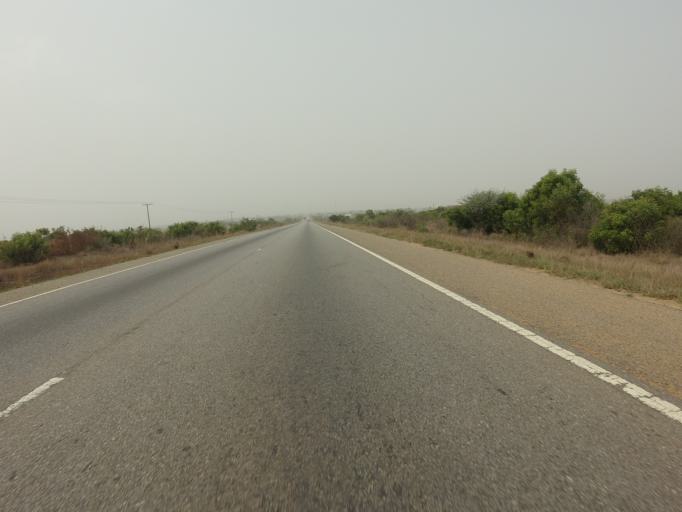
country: GH
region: Greater Accra
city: Tema
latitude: 5.8685
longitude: 0.3098
